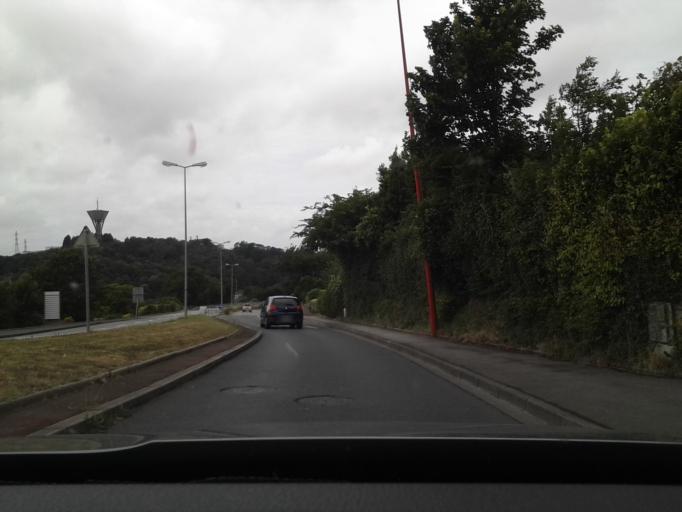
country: FR
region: Lower Normandy
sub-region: Departement de la Manche
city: Cherbourg-Octeville
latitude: 49.6200
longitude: -1.6132
